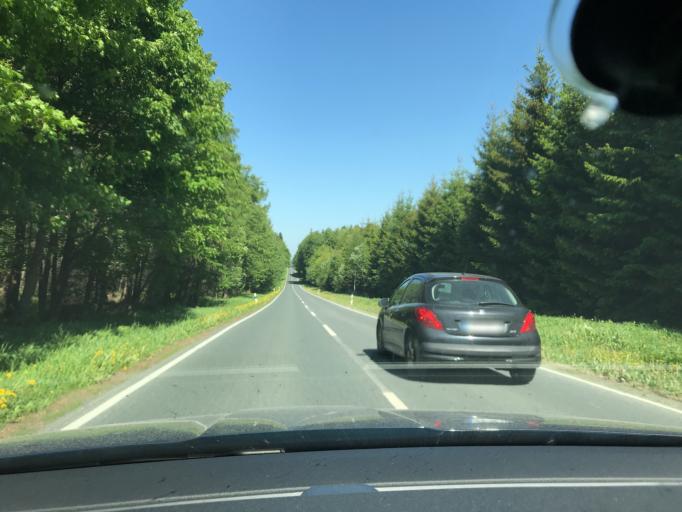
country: DE
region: Saxony
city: Kurort Oberwiesenthal
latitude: 50.4533
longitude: 13.0031
